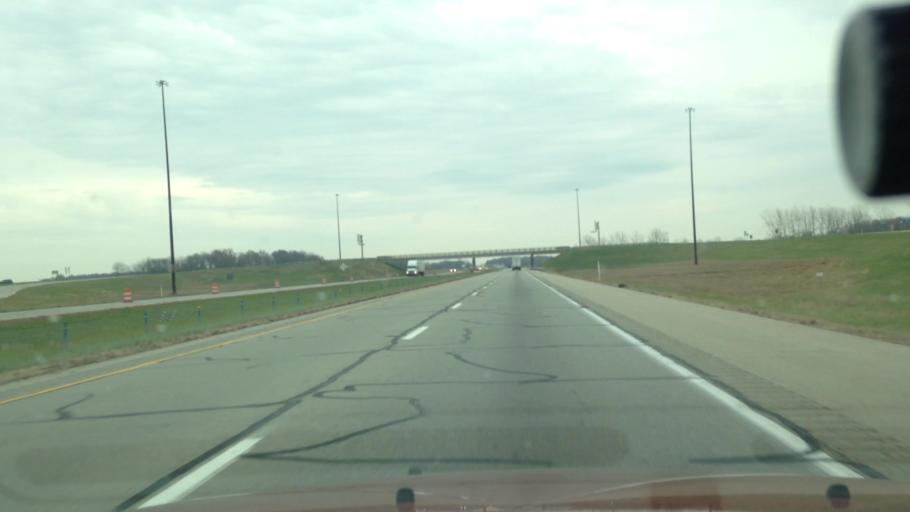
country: US
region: Indiana
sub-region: Wayne County
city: Cambridge City
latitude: 39.8520
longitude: -85.2667
